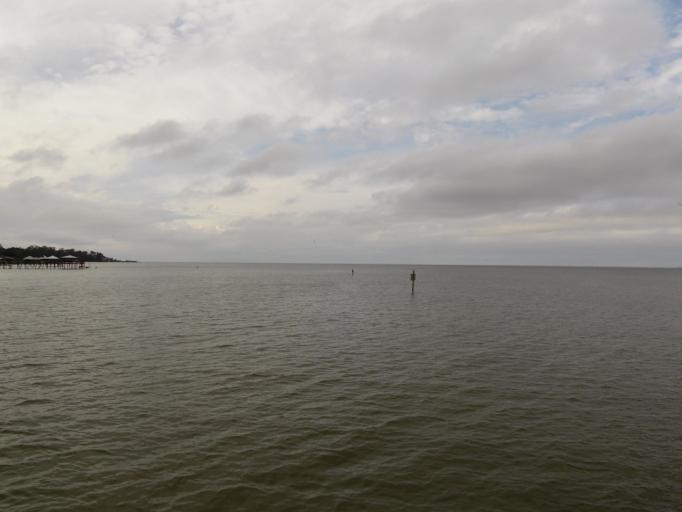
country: US
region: Alabama
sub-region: Baldwin County
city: Fairhope
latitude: 30.5244
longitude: -87.9131
